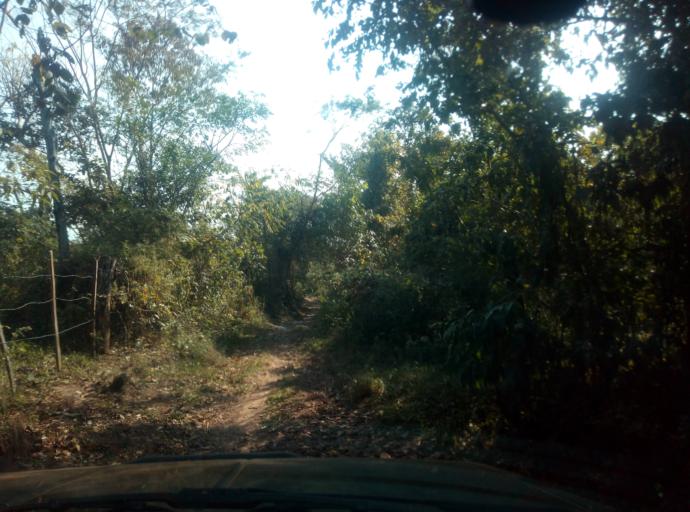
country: PY
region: Caaguazu
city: San Joaquin
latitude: -25.1572
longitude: -56.1275
